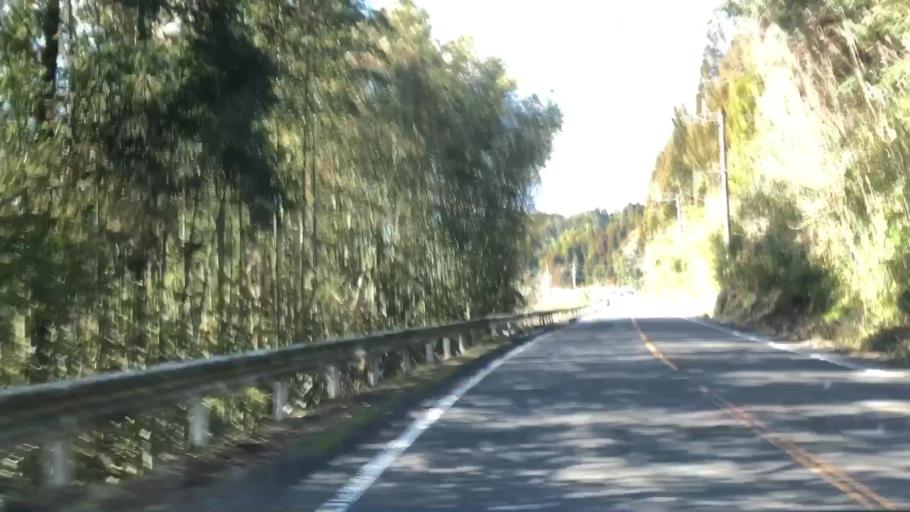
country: JP
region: Kagoshima
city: Satsumasendai
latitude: 31.8600
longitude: 130.4037
